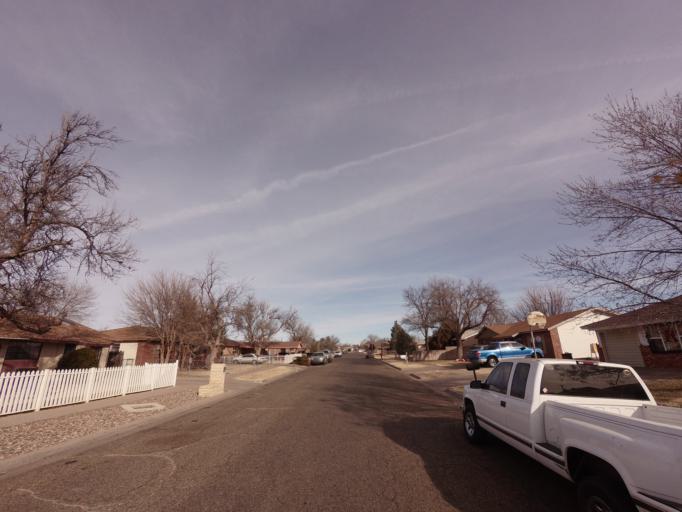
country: US
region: New Mexico
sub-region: Curry County
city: Clovis
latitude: 34.4146
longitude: -103.2220
